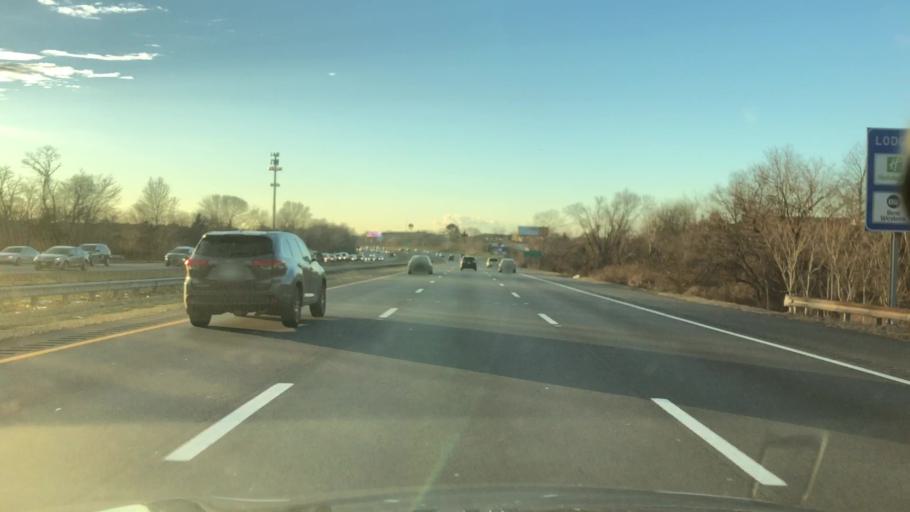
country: US
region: New Jersey
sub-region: Middlesex County
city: South Plainfield
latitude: 40.5551
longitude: -74.4173
